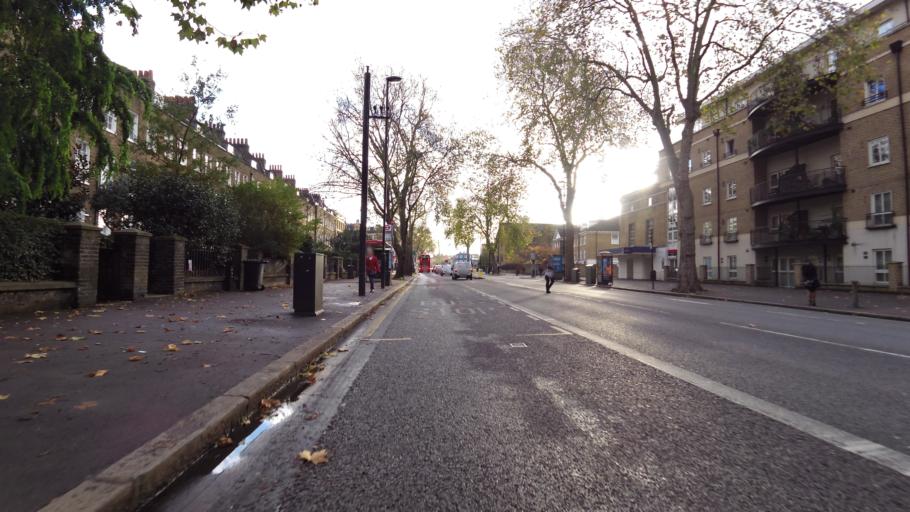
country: GB
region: England
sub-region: Greater London
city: Kennington
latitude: 51.4900
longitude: -0.1111
